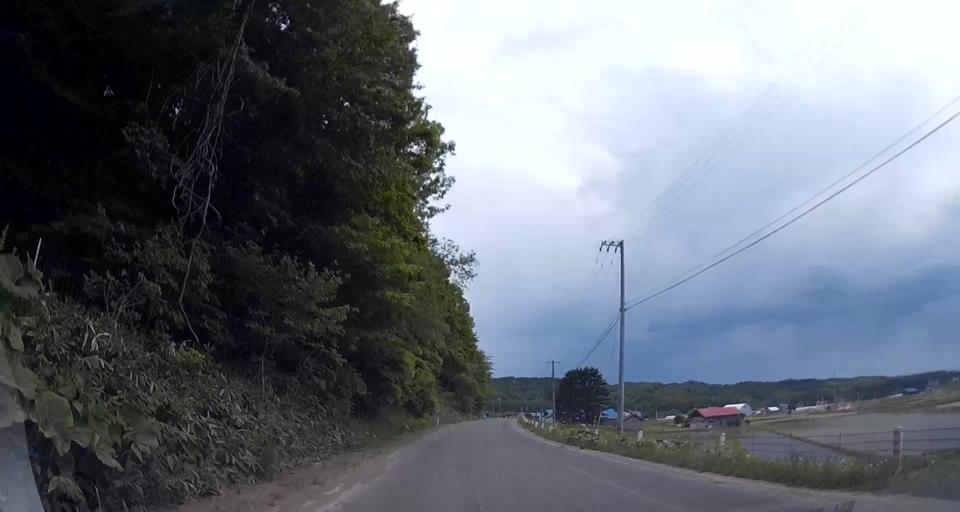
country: JP
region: Hokkaido
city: Chitose
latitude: 42.7577
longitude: 141.9790
